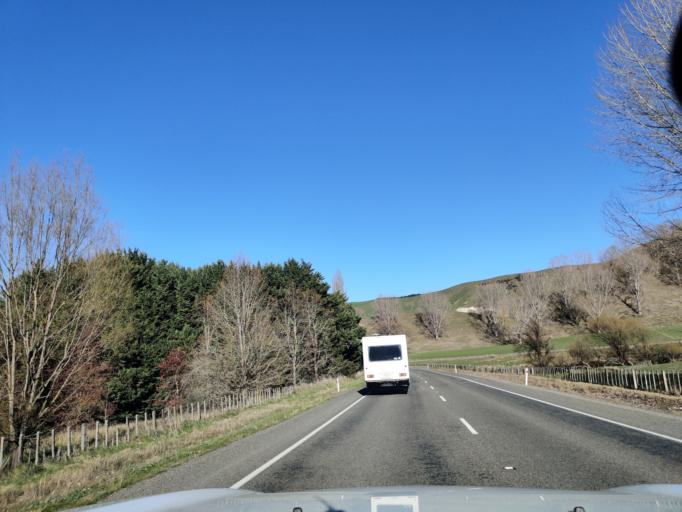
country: NZ
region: Manawatu-Wanganui
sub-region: Ruapehu District
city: Waiouru
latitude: -39.7414
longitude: 175.8378
